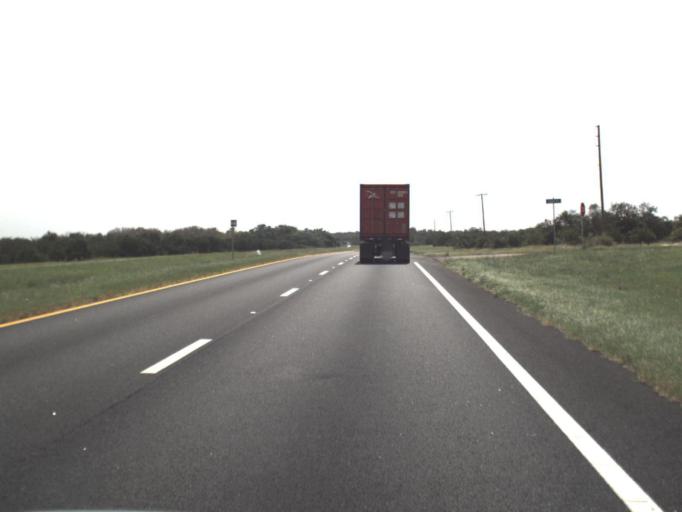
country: US
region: Florida
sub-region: Highlands County
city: Avon Park
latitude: 27.6543
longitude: -81.5367
